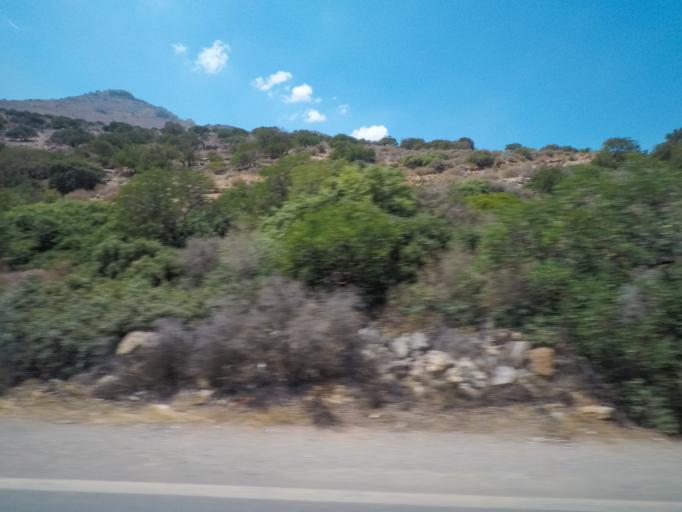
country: GR
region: Crete
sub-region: Nomos Lasithiou
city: Skhisma
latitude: 35.2486
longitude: 25.7242
